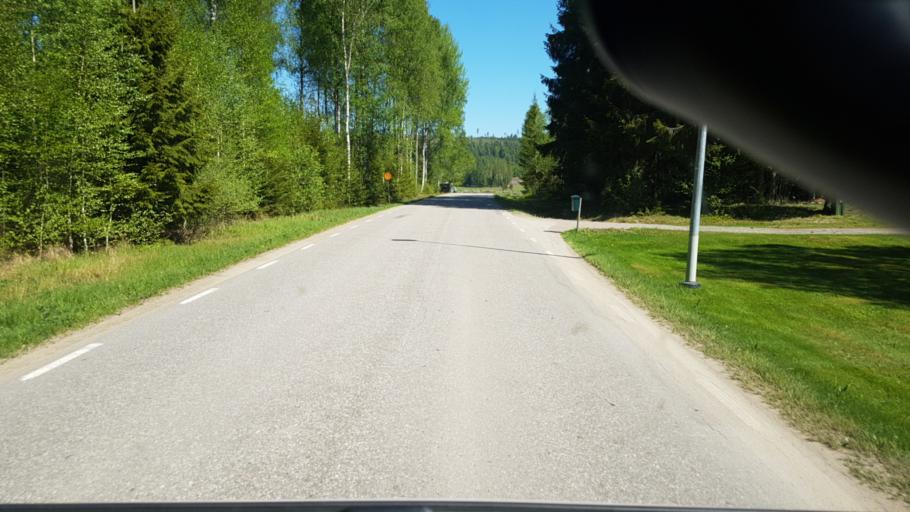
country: SE
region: Vaermland
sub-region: Arvika Kommun
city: Arvika
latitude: 59.8204
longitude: 12.5727
